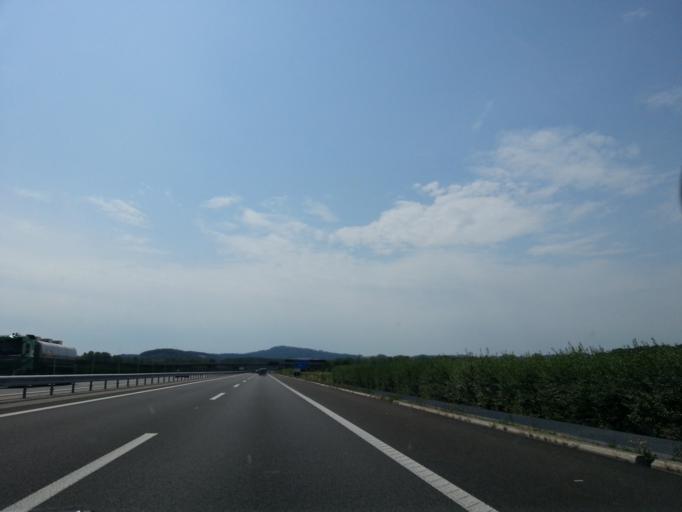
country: CH
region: Vaud
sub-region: Broye-Vully District
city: Payerne
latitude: 46.8373
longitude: 6.9225
